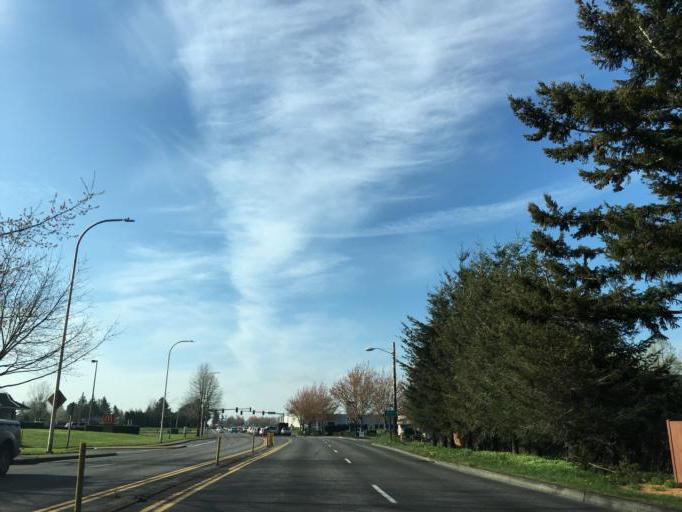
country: US
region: Oregon
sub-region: Multnomah County
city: Wood Village
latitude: 45.5295
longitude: -122.4131
